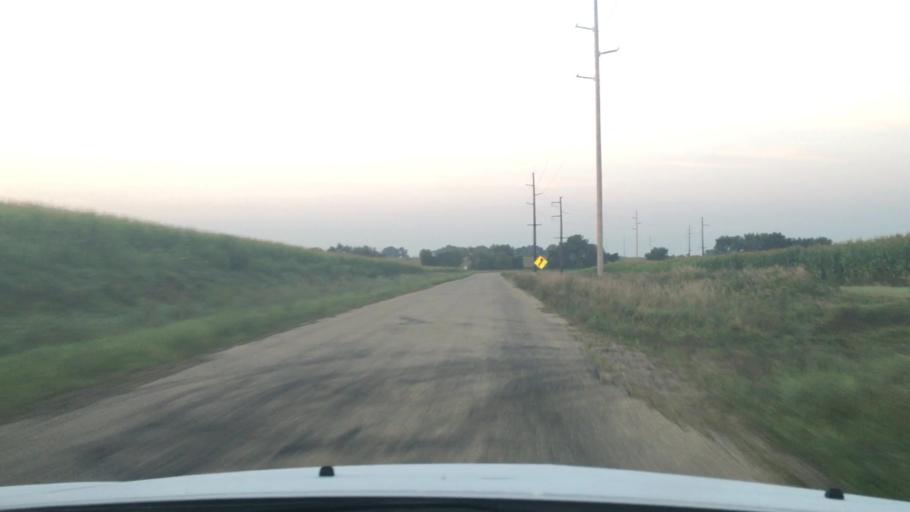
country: US
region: Illinois
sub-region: Ogle County
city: Rochelle
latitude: 41.8944
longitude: -88.9997
